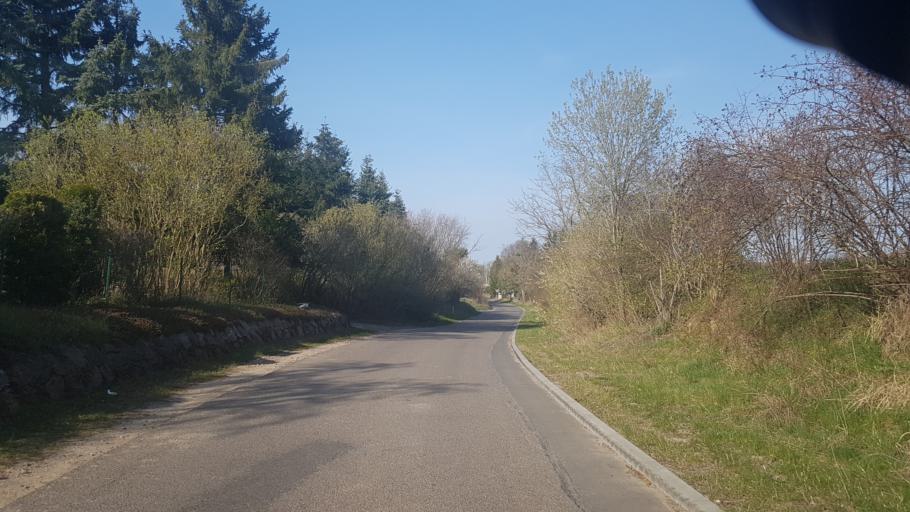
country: DE
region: Brandenburg
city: Gerswalde
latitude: 53.2127
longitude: 13.7857
